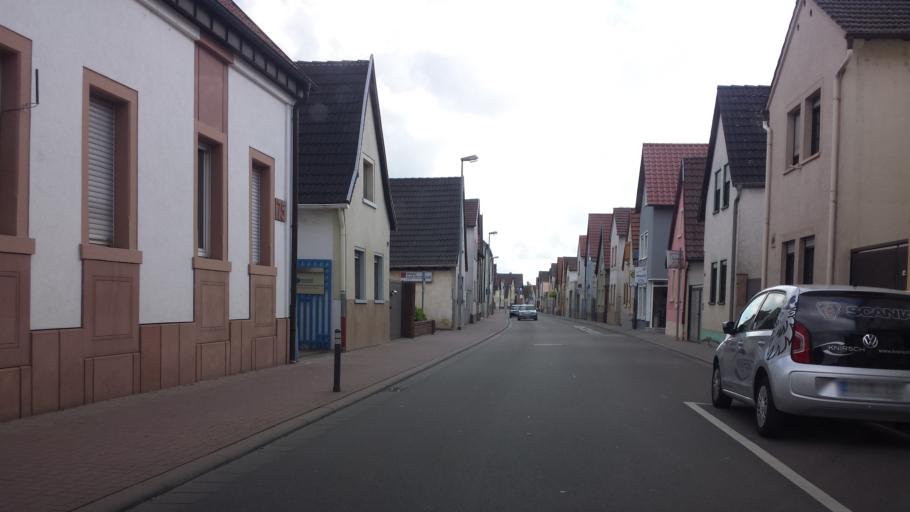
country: DE
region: Rheinland-Pfalz
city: Dannstadt-Schauernheim
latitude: 49.4278
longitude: 8.3145
